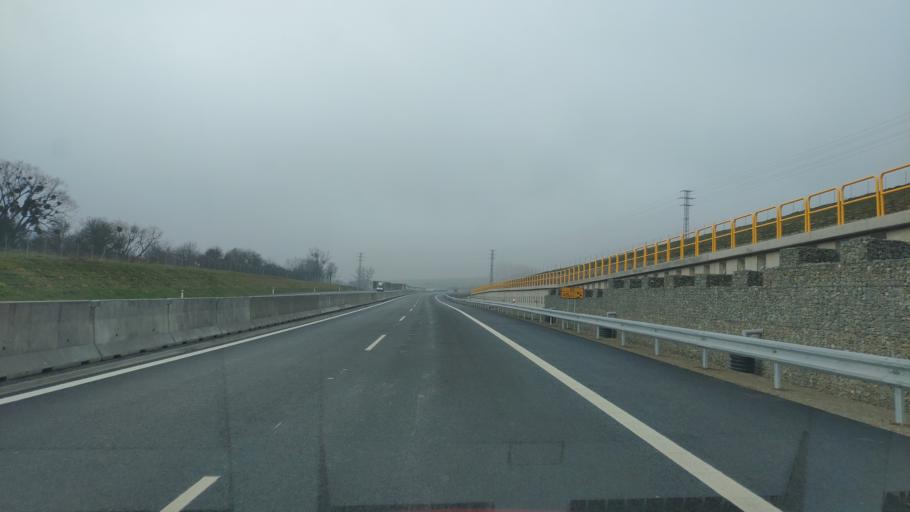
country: SK
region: Kosicky
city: Kosice
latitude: 48.7426
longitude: 21.3714
